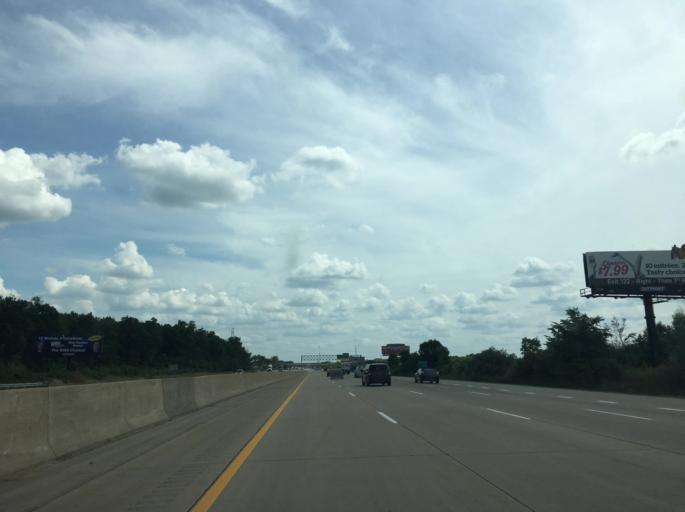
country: US
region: Michigan
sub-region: Genesee County
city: Mount Morris
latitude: 43.1126
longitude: -83.7635
